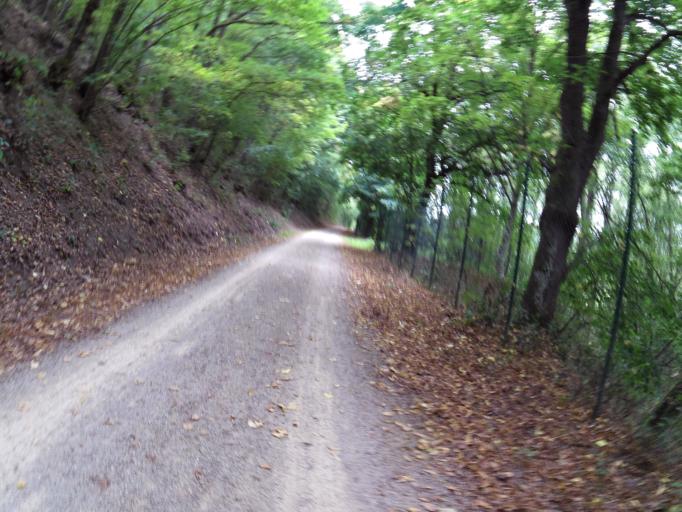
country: DE
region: North Rhine-Westphalia
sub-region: Regierungsbezirk Koln
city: Schleiden
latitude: 50.5776
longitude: 6.4699
